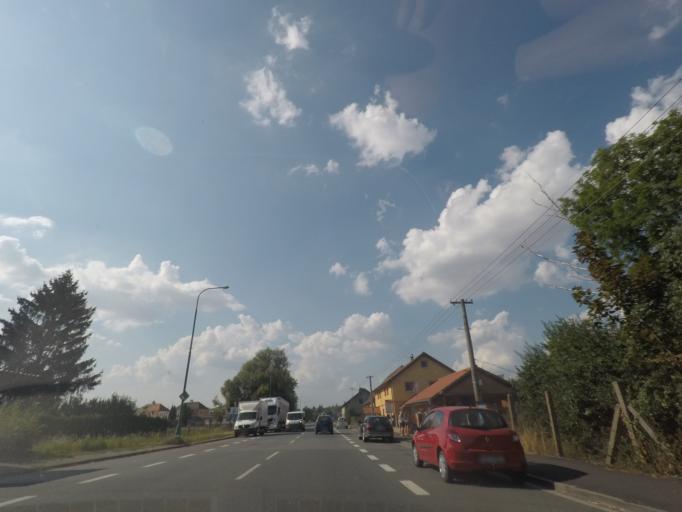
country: CZ
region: Kralovehradecky
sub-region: Okres Nachod
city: Jaromer
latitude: 50.3526
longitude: 15.9083
